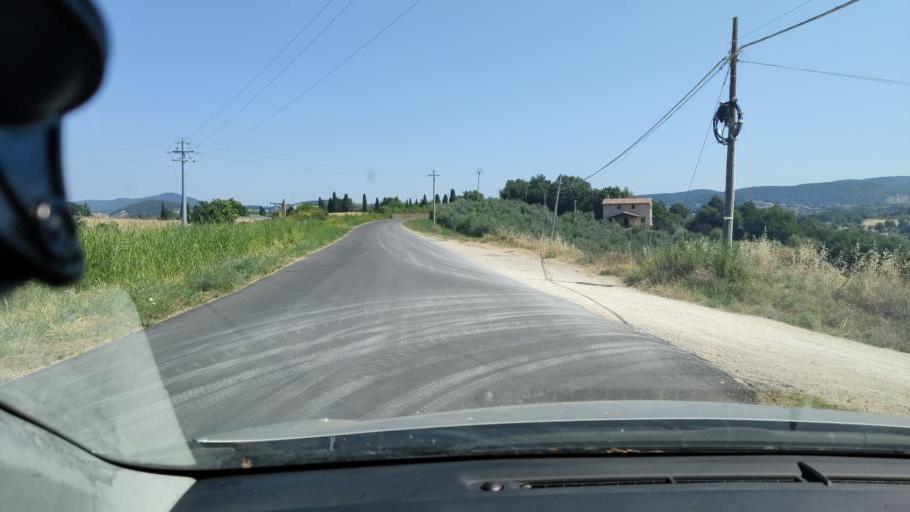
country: IT
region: Umbria
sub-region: Provincia di Terni
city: Fornole
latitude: 42.5200
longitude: 12.4328
